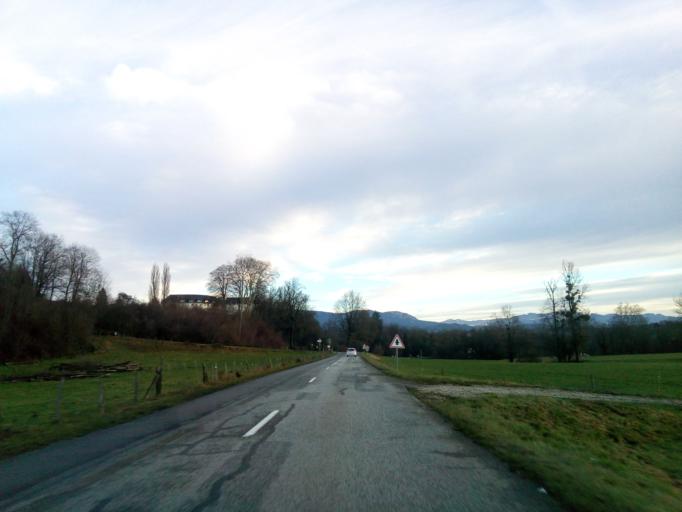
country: FR
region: Rhone-Alpes
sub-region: Departement de la Savoie
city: Le Pont-de-Beauvoisin
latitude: 45.5621
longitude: 5.6730
